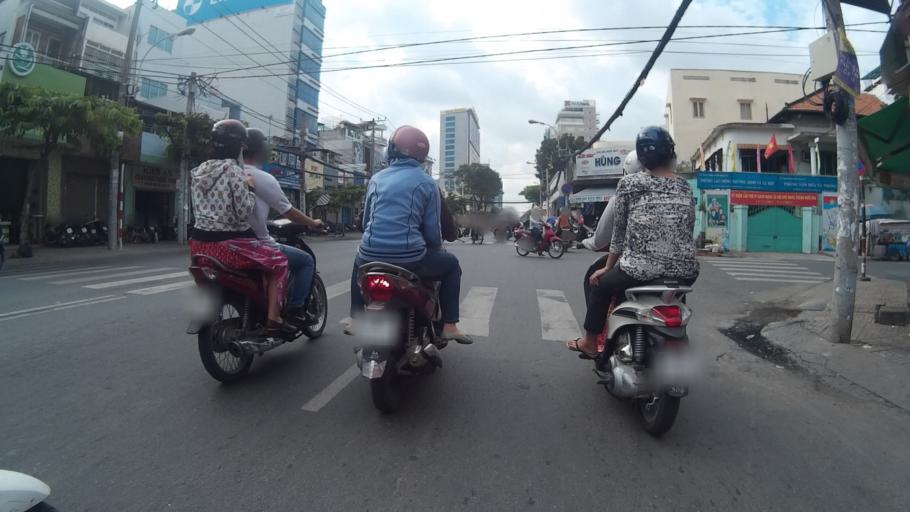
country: VN
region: Ho Chi Minh City
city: Quan Ba
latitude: 10.7746
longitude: 106.6877
